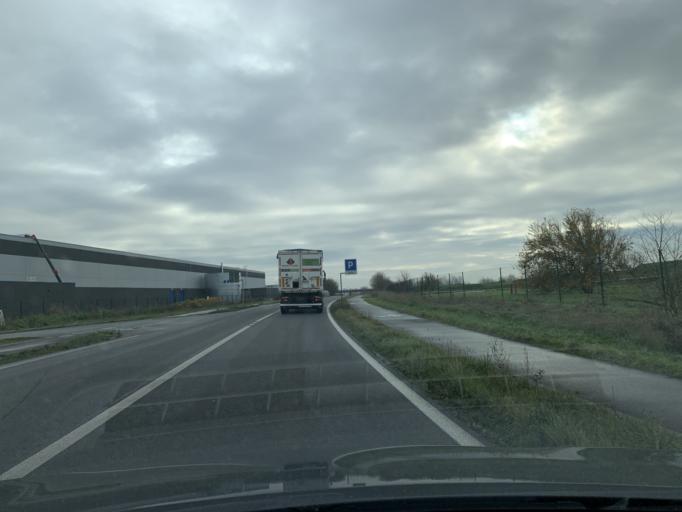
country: FR
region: Nord-Pas-de-Calais
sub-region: Departement du Nord
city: Neuville-Saint-Remy
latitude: 50.1989
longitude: 3.2037
